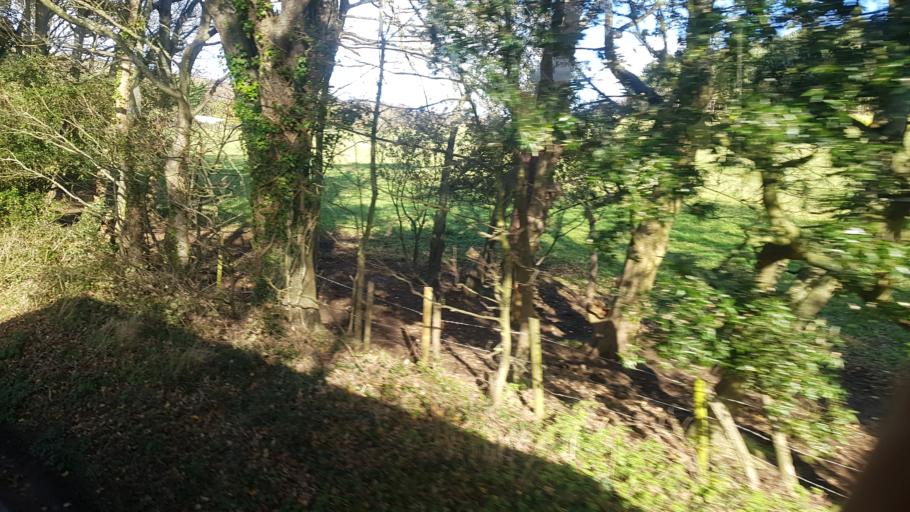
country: GB
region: England
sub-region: Isle of Wight
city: Shalfleet
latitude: 50.6492
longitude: -1.4172
